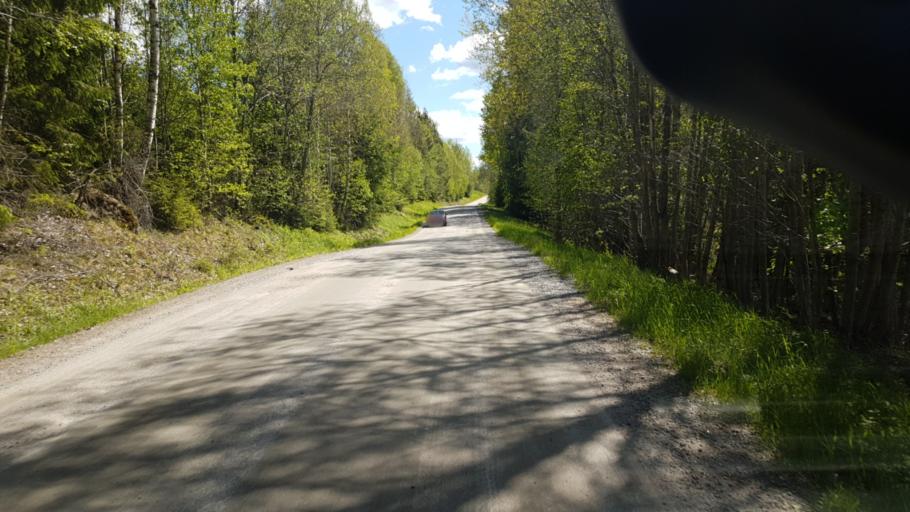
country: SE
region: Vaermland
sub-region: Sunne Kommun
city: Sunne
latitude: 59.6773
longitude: 12.9001
